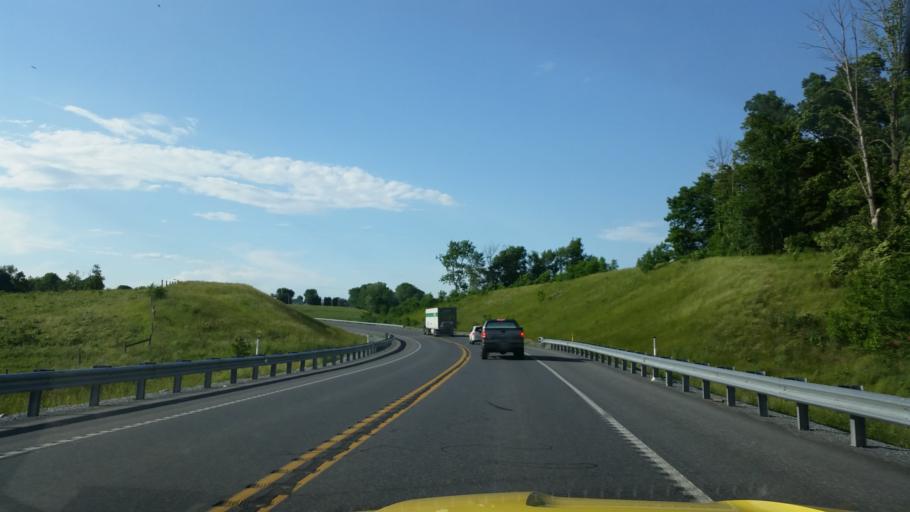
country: US
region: Pennsylvania
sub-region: Lancaster County
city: Brickerville
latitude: 40.2917
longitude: -76.3030
